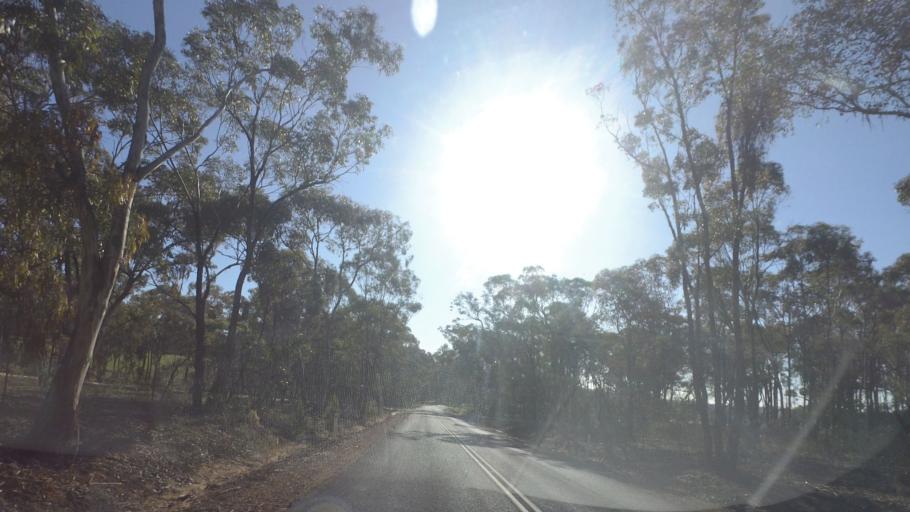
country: AU
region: Victoria
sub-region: Greater Bendigo
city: Kangaroo Flat
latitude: -36.8654
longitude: 144.2836
